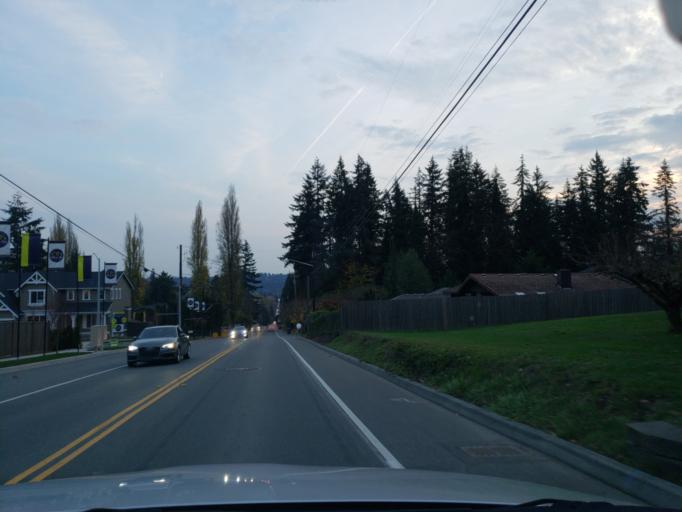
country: US
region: Washington
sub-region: King County
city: Kenmore
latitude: 47.7793
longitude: -122.2330
